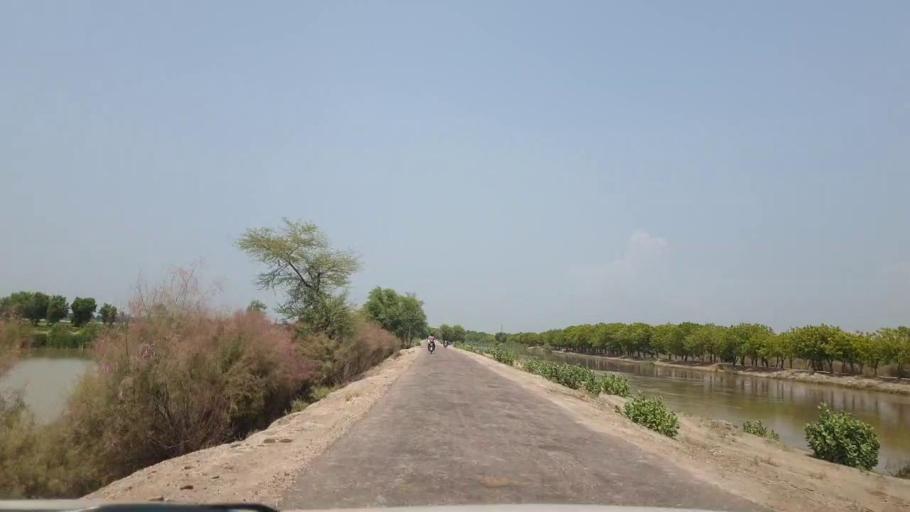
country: PK
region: Sindh
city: Dokri
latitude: 27.3521
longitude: 68.1126
